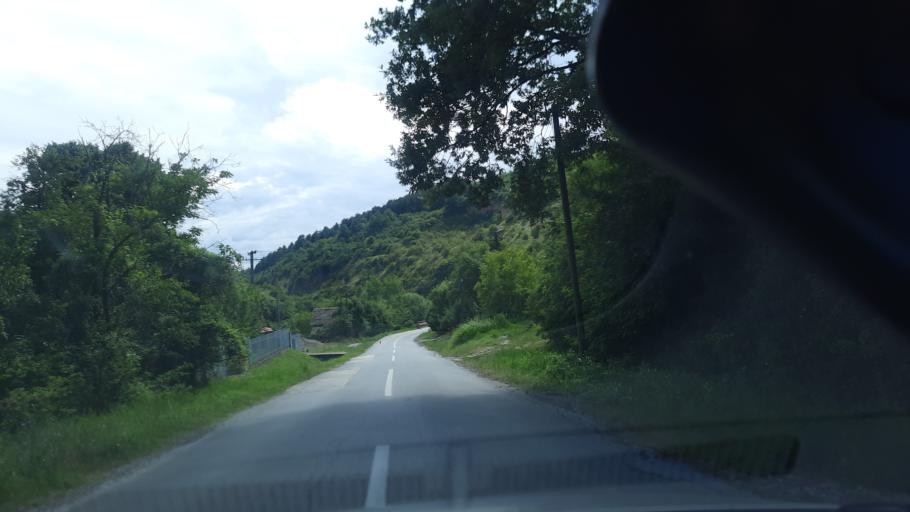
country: RS
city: Celarevo
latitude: 45.1326
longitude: 19.5761
